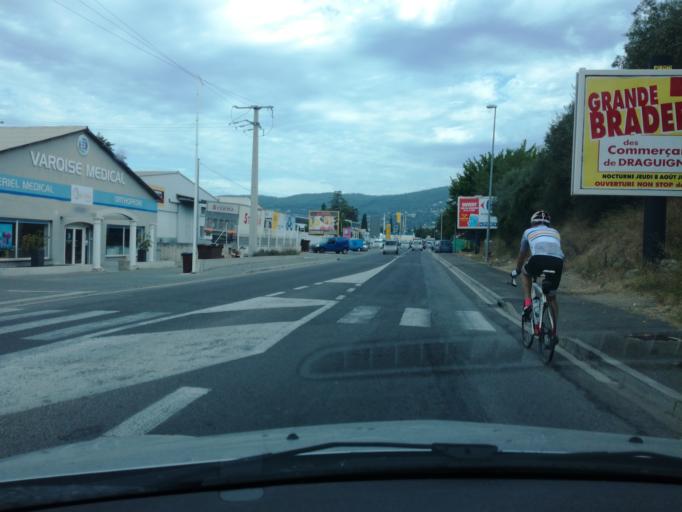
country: FR
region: Provence-Alpes-Cote d'Azur
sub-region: Departement du Var
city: Draguignan
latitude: 43.5284
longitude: 6.4490
